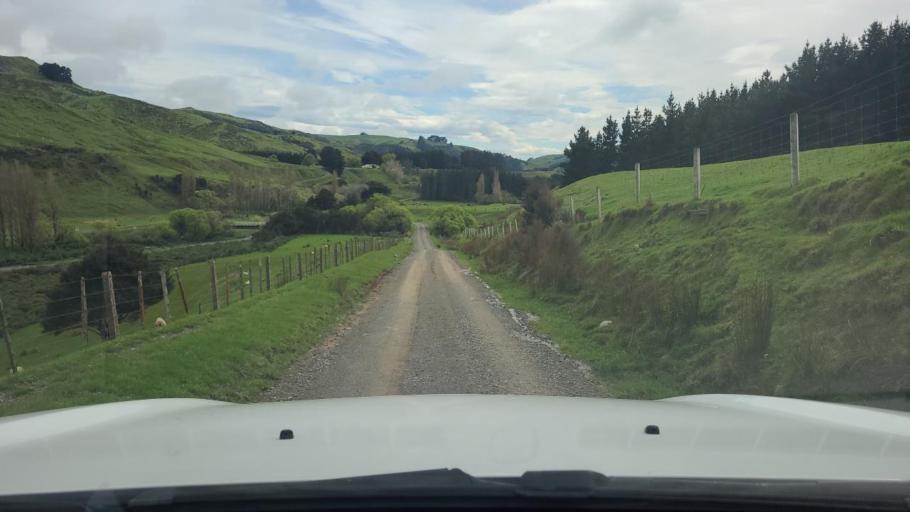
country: NZ
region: Wellington
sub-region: South Wairarapa District
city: Waipawa
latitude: -41.3892
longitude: 175.4524
